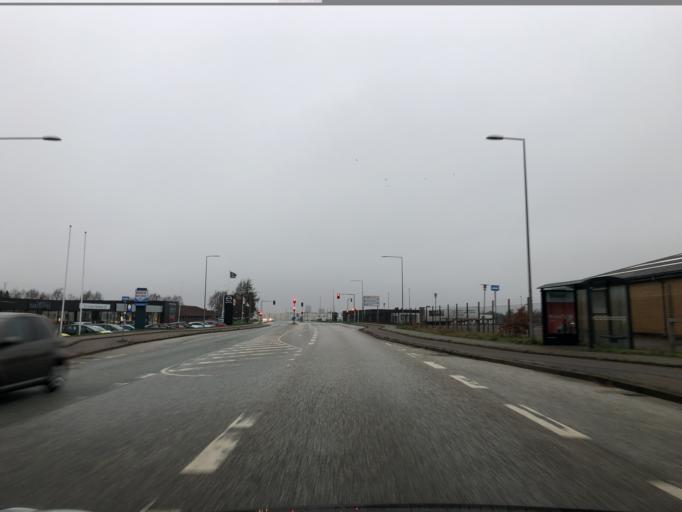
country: DK
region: Central Jutland
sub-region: Herning Kommune
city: Lind
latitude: 56.1084
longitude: 8.9790
